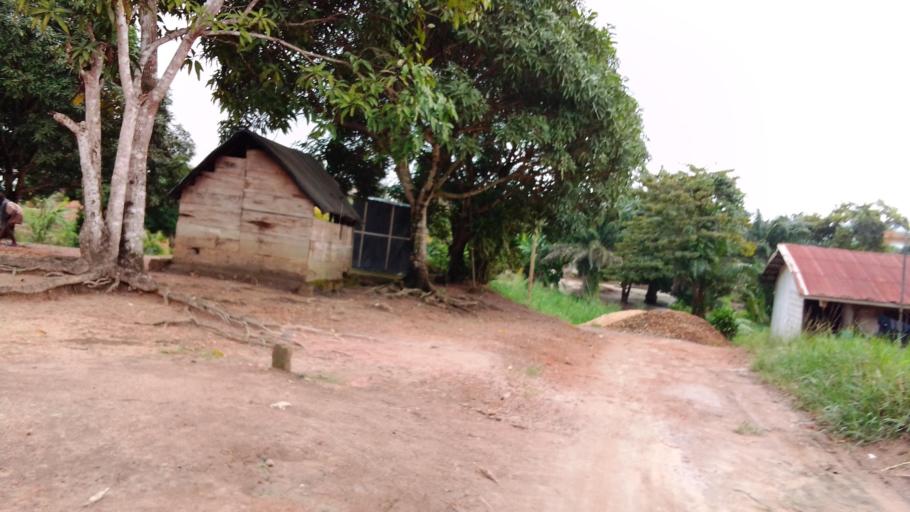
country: SL
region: Eastern Province
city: Kenema
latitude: 7.8784
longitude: -11.1639
